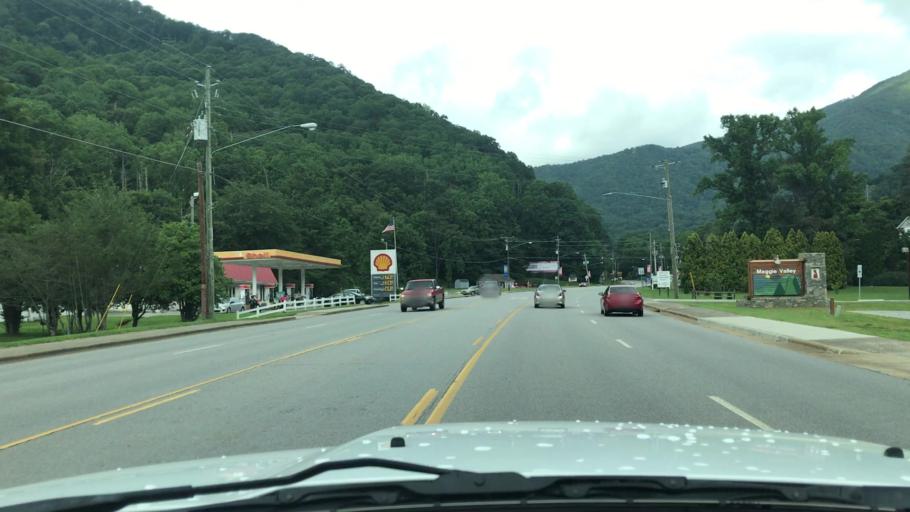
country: US
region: North Carolina
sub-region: Haywood County
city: Maggie Valley
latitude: 35.5189
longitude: -83.1043
